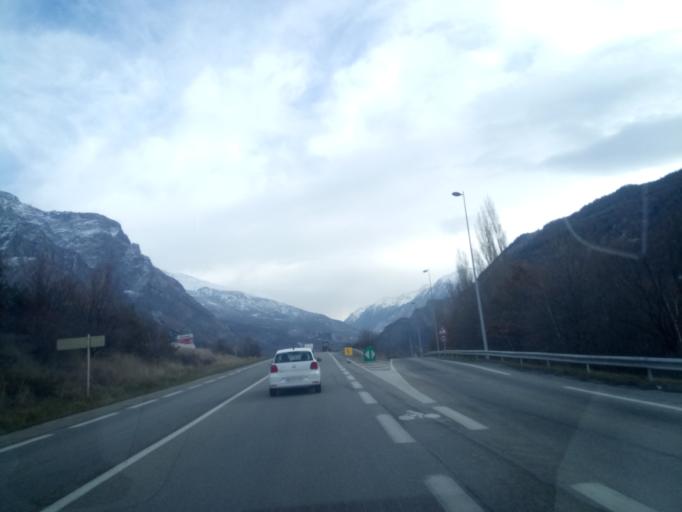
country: FR
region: Rhone-Alpes
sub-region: Departement de la Savoie
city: Villargondran
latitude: 45.2535
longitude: 6.3971
